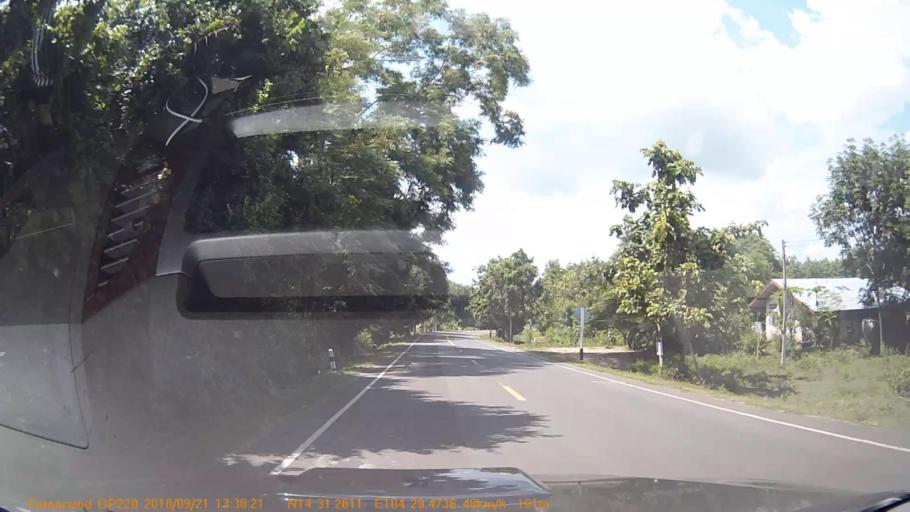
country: TH
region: Sisaket
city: Khun Han
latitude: 14.5217
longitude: 104.4911
